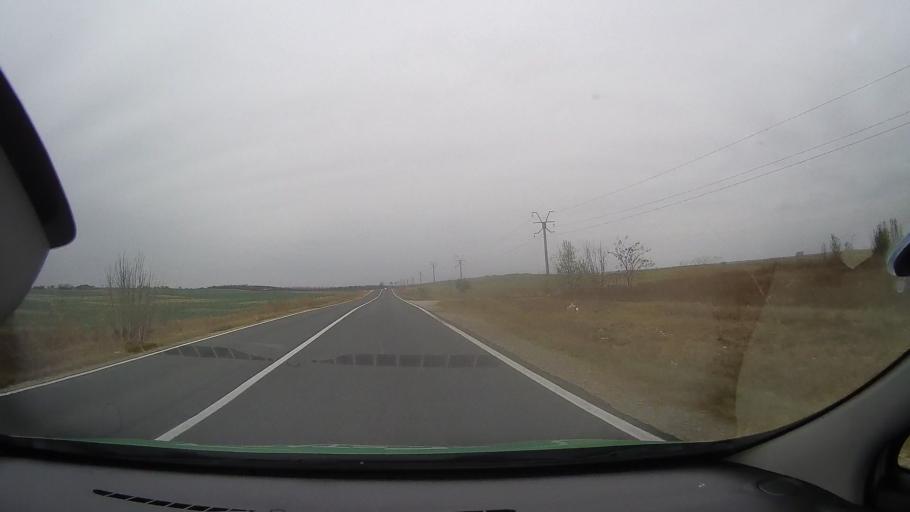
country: RO
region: Constanta
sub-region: Oras Harsova
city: Harsova
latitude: 44.6937
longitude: 27.9382
